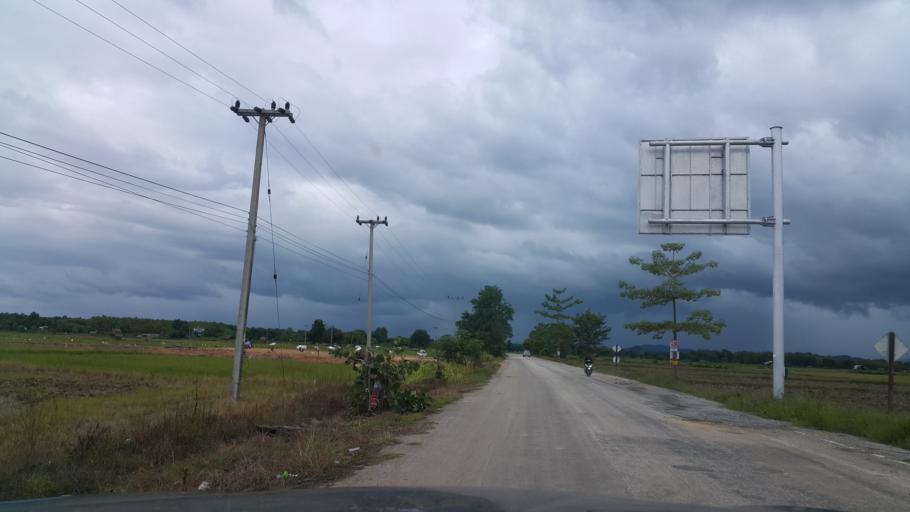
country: TH
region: Sukhothai
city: Thung Saliam
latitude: 17.3139
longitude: 99.5777
